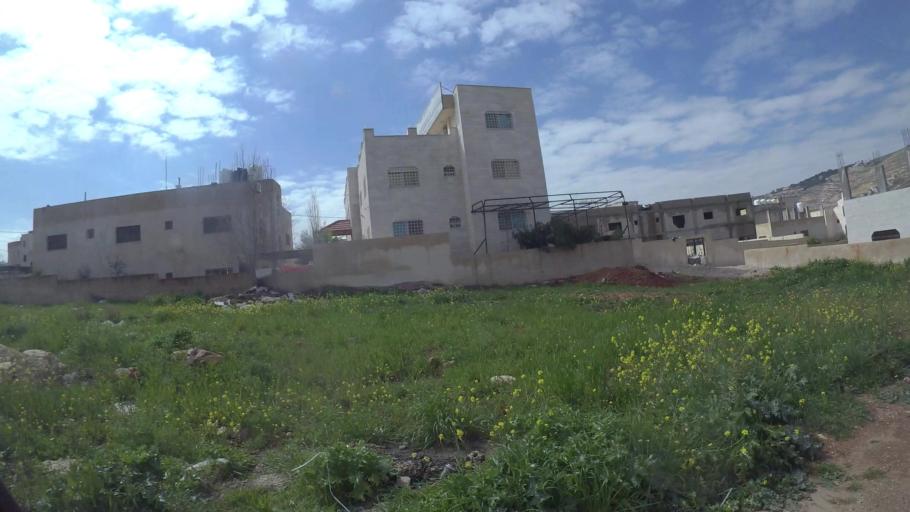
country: JO
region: Amman
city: Al Jubayhah
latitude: 32.0653
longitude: 35.8228
